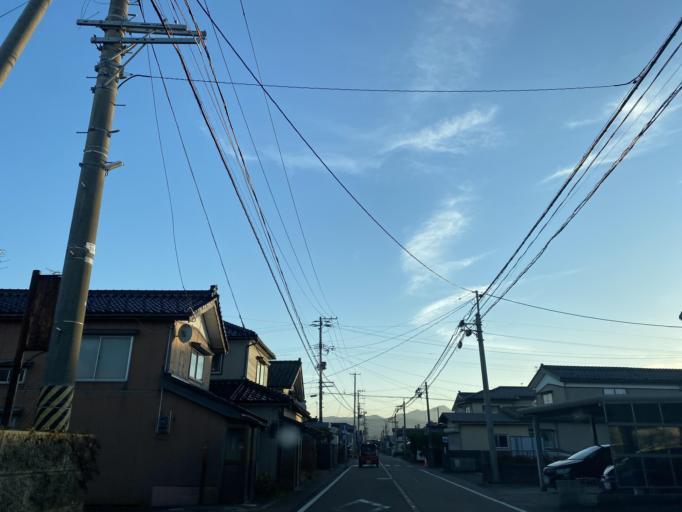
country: JP
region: Niigata
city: Kashiwazaki
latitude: 37.3788
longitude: 138.5664
